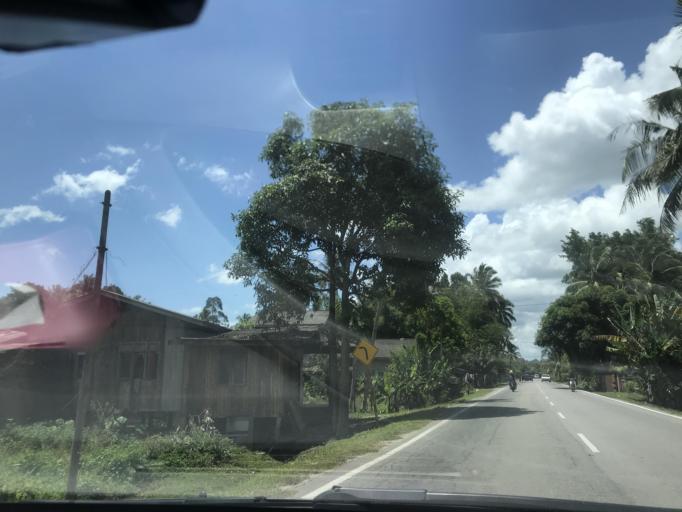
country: MY
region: Kelantan
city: Tumpat
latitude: 6.1944
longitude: 102.1415
